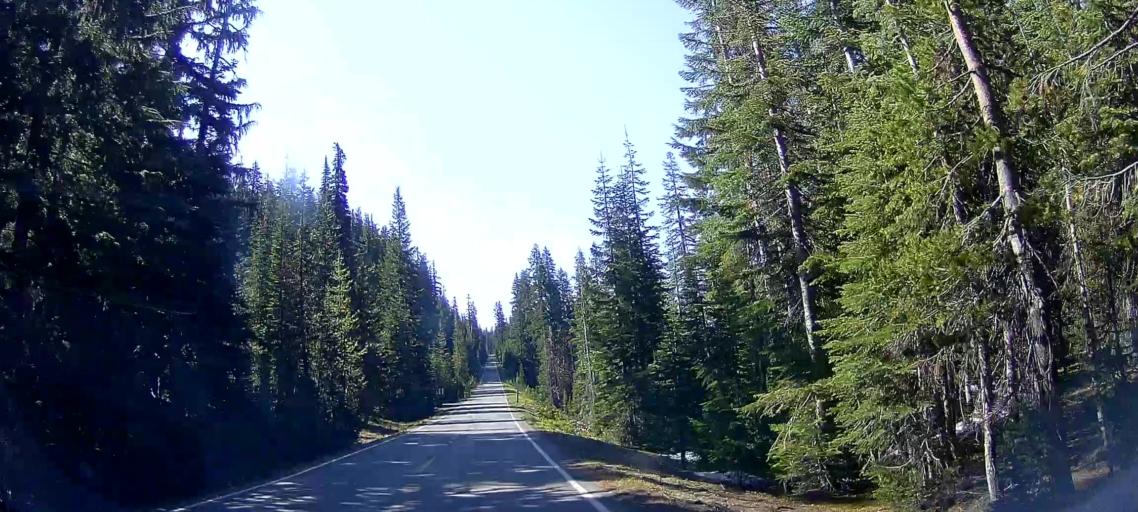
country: US
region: Oregon
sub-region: Jackson County
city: Shady Cove
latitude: 42.8903
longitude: -122.1321
